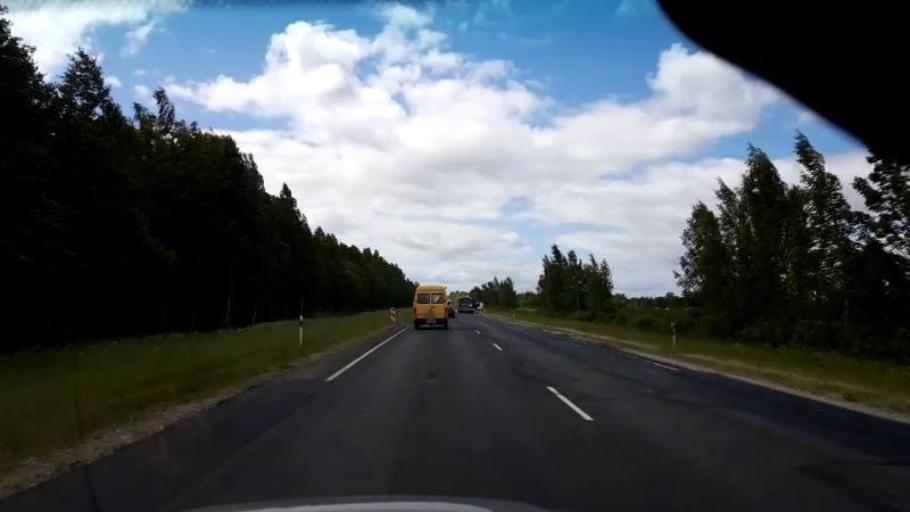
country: LV
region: Salacgrivas
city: Ainazi
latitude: 57.9996
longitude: 24.4790
